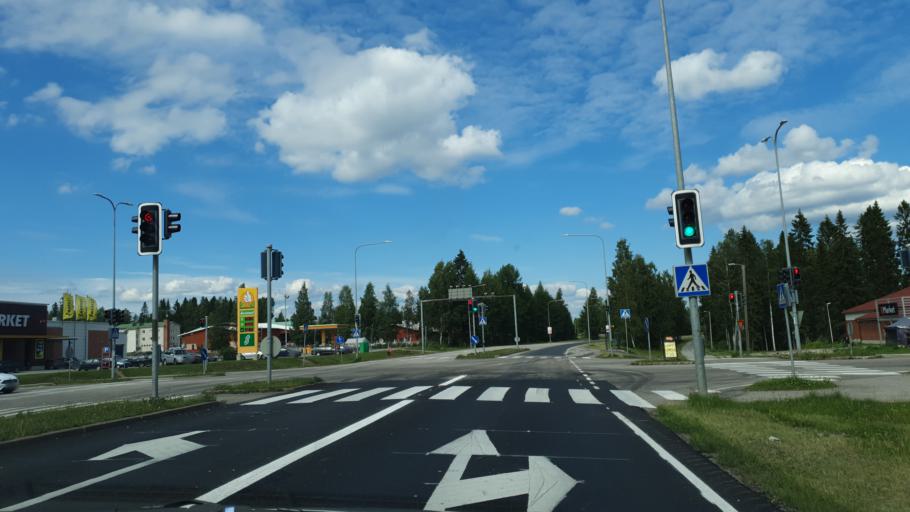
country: FI
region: Kainuu
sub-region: Kajaani
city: Kajaani
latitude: 64.2372
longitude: 27.7488
